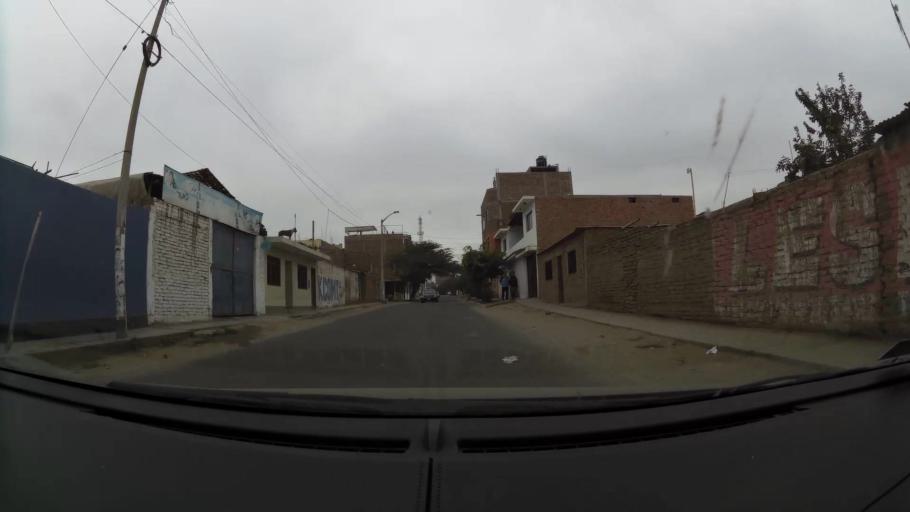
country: PE
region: La Libertad
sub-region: Provincia de Trujillo
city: La Esperanza
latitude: -8.0811
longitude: -79.0492
